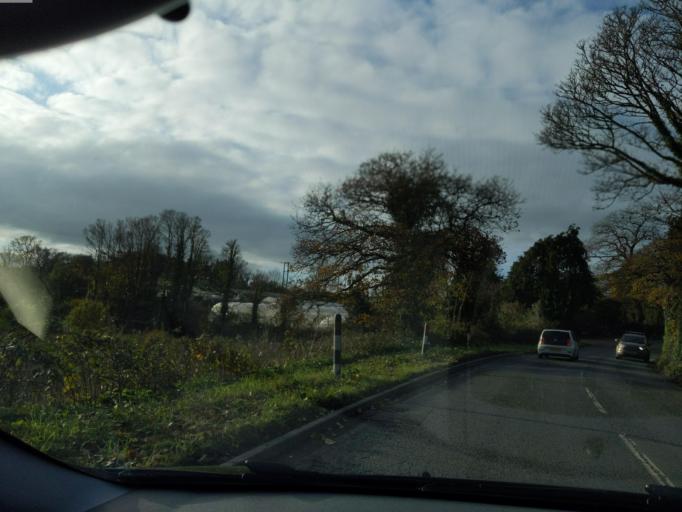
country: GB
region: England
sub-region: Cornwall
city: Padstow
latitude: 50.5116
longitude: -4.9403
